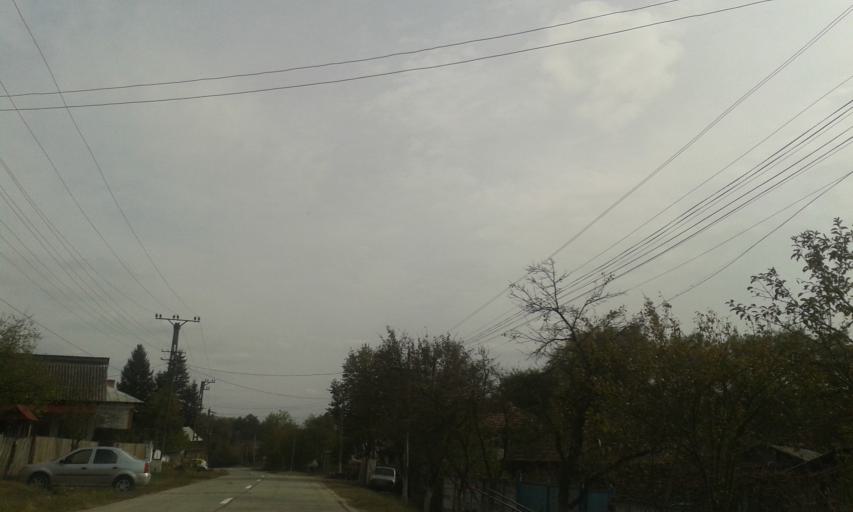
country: RO
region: Valcea
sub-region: Comuna Gradistea
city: Gradistea
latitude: 44.9104
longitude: 23.7869
